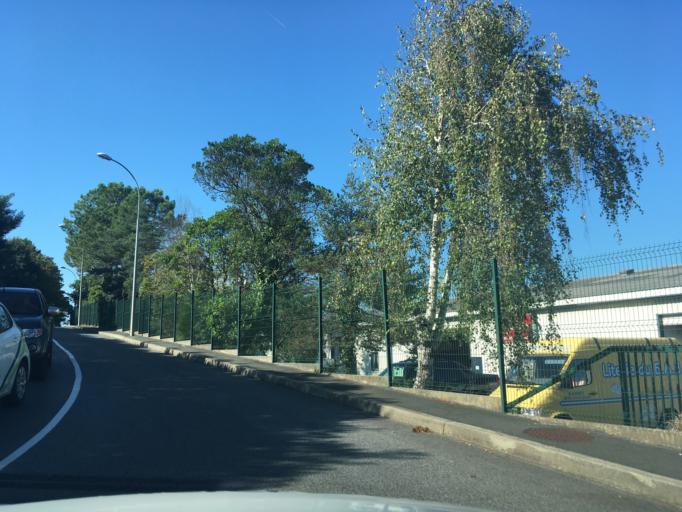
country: FR
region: Aquitaine
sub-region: Departement des Pyrenees-Atlantiques
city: Biarritz
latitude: 43.4677
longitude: -1.5435
